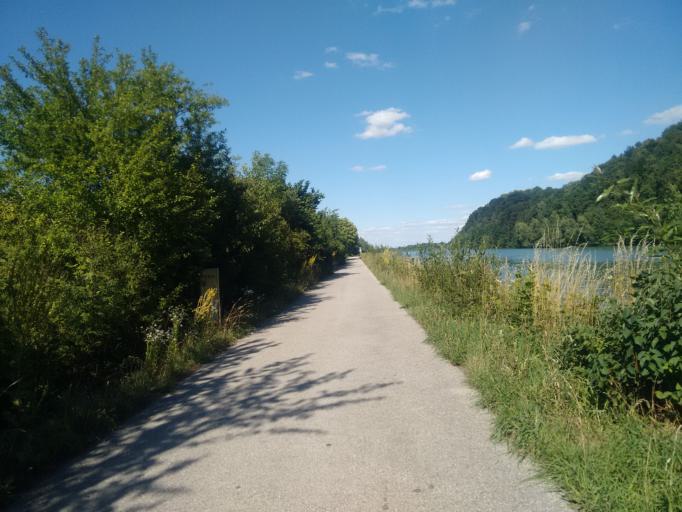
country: AT
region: Upper Austria
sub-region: Wels Stadt
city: Wels
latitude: 48.1597
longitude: 14.0590
